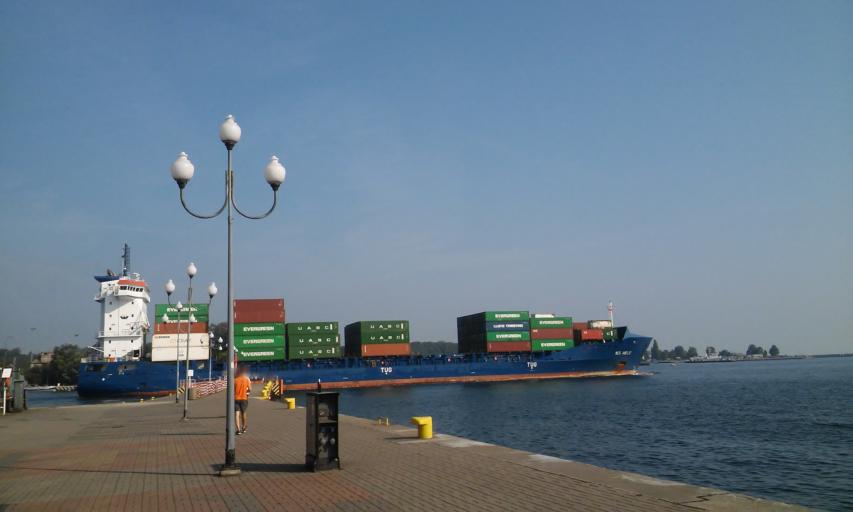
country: PL
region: Pomeranian Voivodeship
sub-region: Gdynia
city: Gdynia
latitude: 54.5336
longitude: 18.5477
